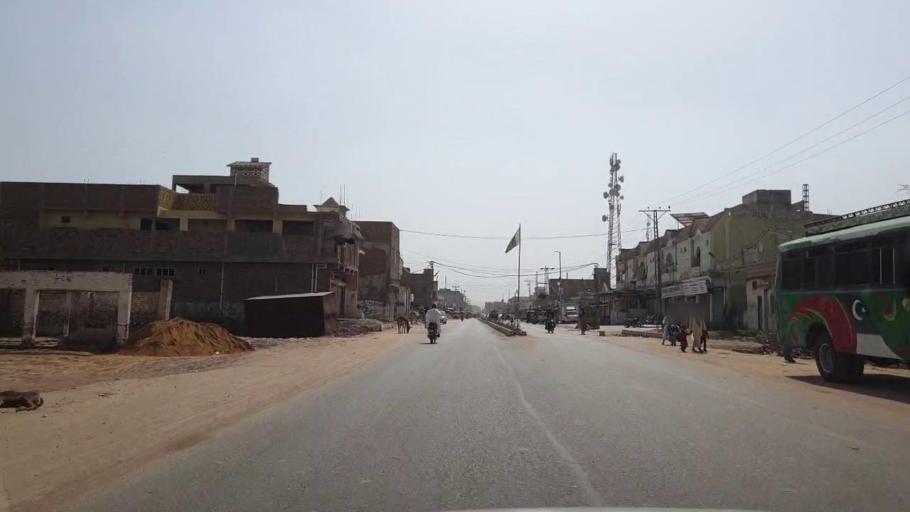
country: PK
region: Sindh
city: Matli
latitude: 25.0488
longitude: 68.6513
